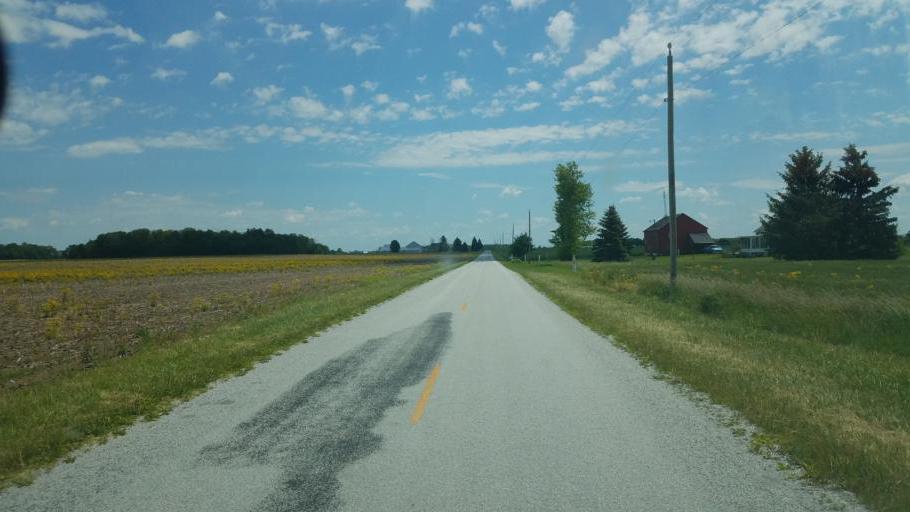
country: US
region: Ohio
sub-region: Hardin County
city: Forest
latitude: 40.6728
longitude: -83.4578
